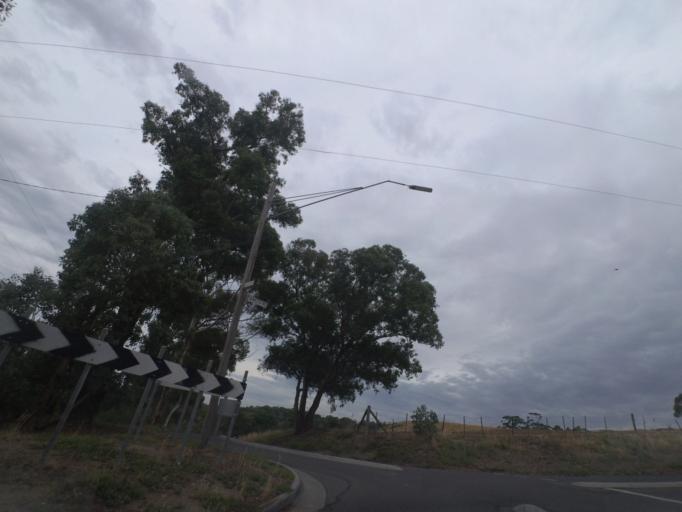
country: AU
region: Victoria
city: Plenty
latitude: -37.6597
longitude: 145.1288
